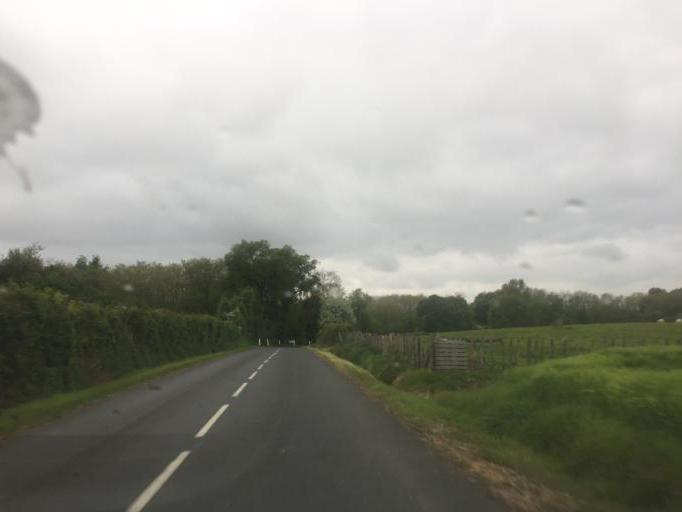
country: FR
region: Rhone-Alpes
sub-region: Departement de l'Ain
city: Reyrieux
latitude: 45.9397
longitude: 4.8317
